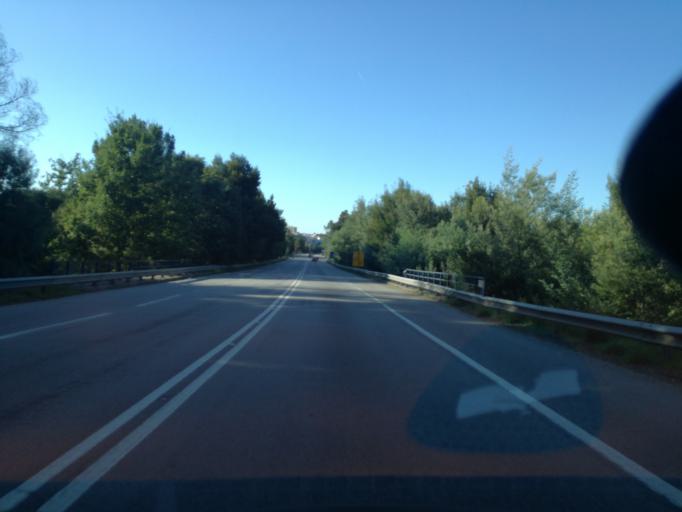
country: PT
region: Porto
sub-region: Santo Tirso
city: Sao Miguel do Couto
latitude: 41.3241
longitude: -8.4692
